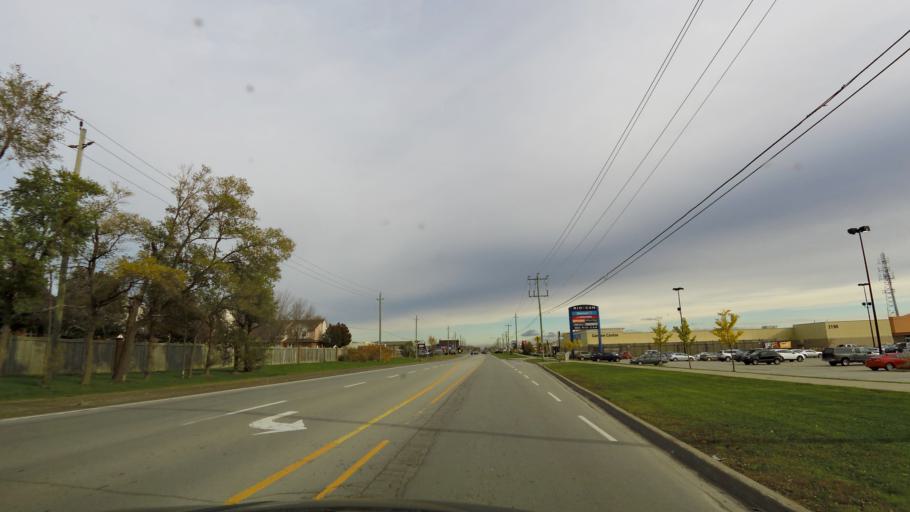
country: CA
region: Ontario
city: Hamilton
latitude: 43.1750
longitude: -79.7845
